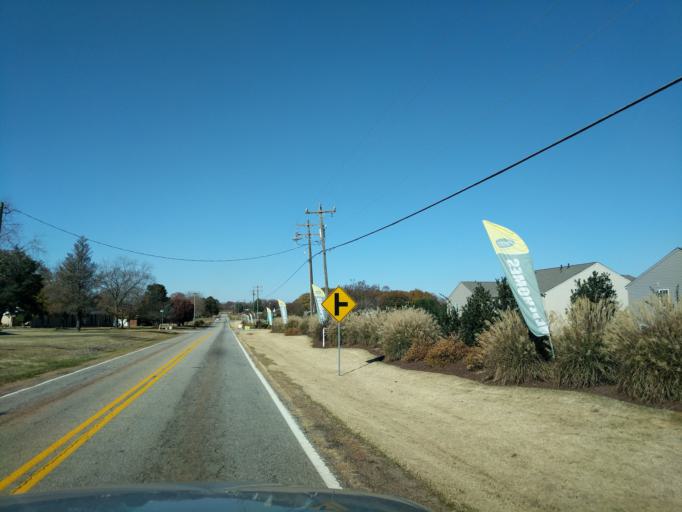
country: US
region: South Carolina
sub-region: Spartanburg County
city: Lyman
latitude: 34.9653
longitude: -82.1413
